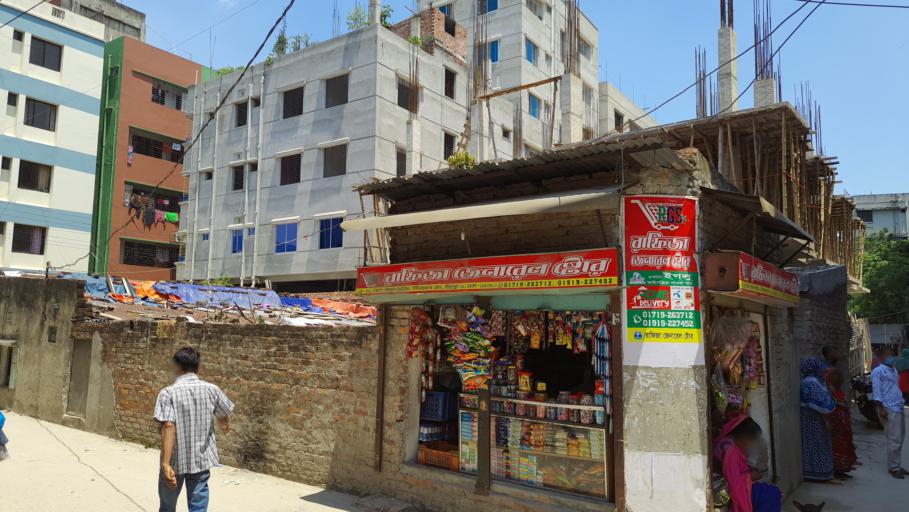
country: BD
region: Dhaka
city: Azimpur
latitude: 23.8113
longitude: 90.3521
